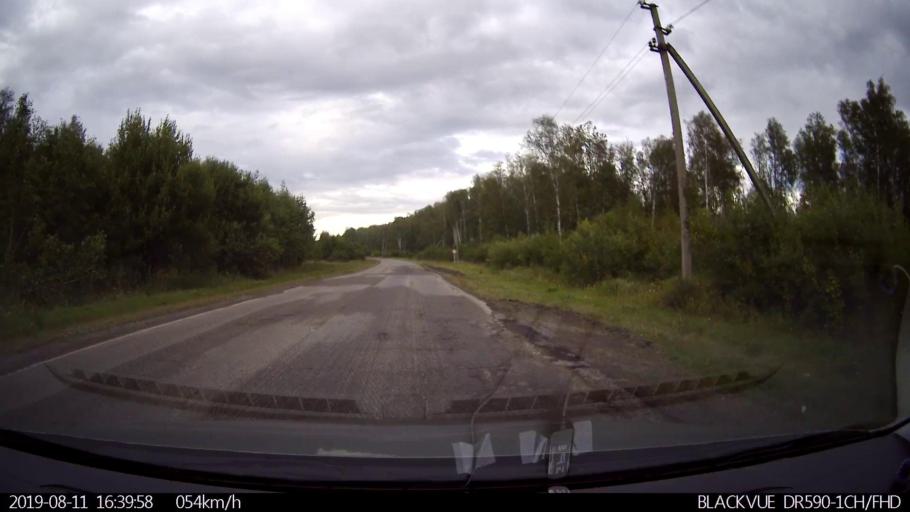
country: RU
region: Ulyanovsk
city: Mayna
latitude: 54.1429
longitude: 47.6418
